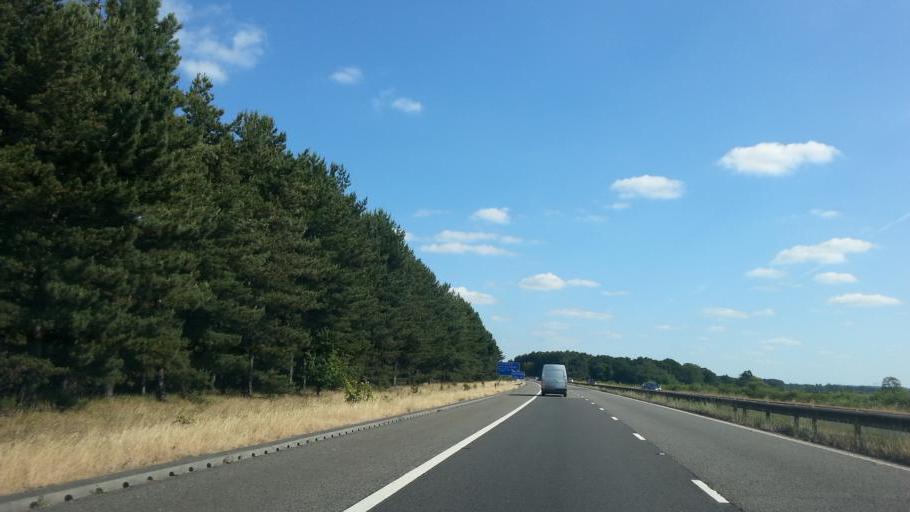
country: GB
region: England
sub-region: Nottinghamshire
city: Bircotes
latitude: 53.4006
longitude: -1.0785
